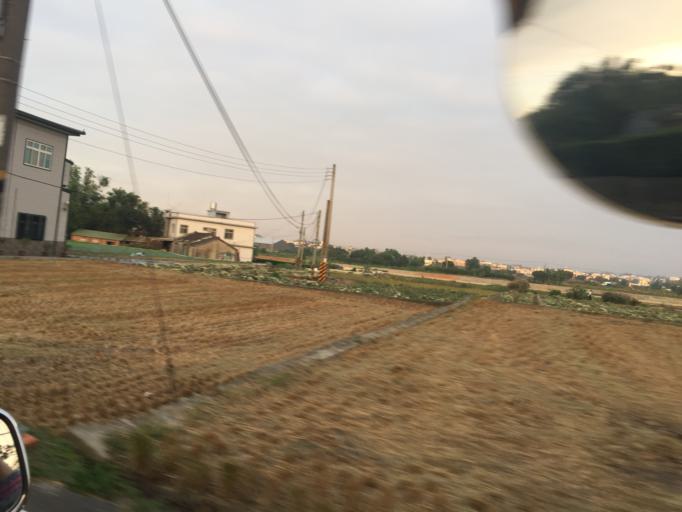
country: TW
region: Taiwan
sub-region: Miaoli
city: Miaoli
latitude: 24.4820
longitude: 120.7771
